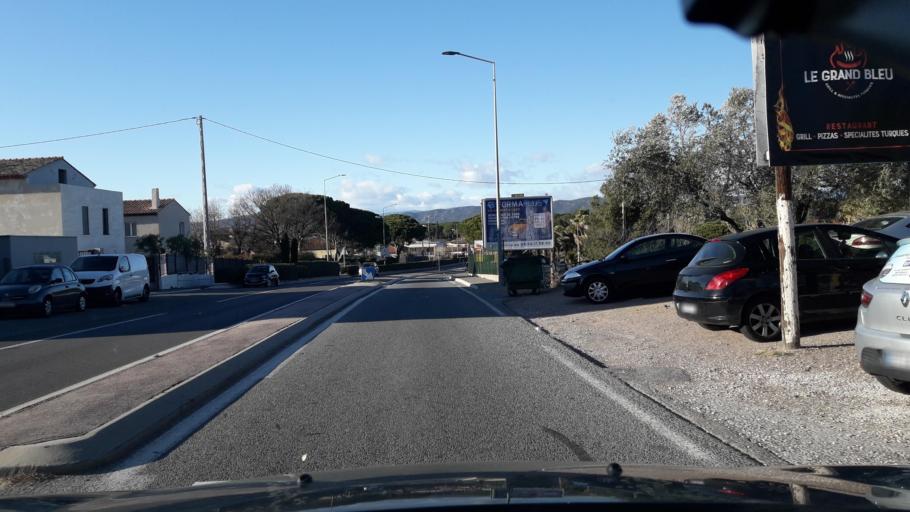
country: FR
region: Provence-Alpes-Cote d'Azur
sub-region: Departement du Var
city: Frejus
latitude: 43.4505
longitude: 6.7275
